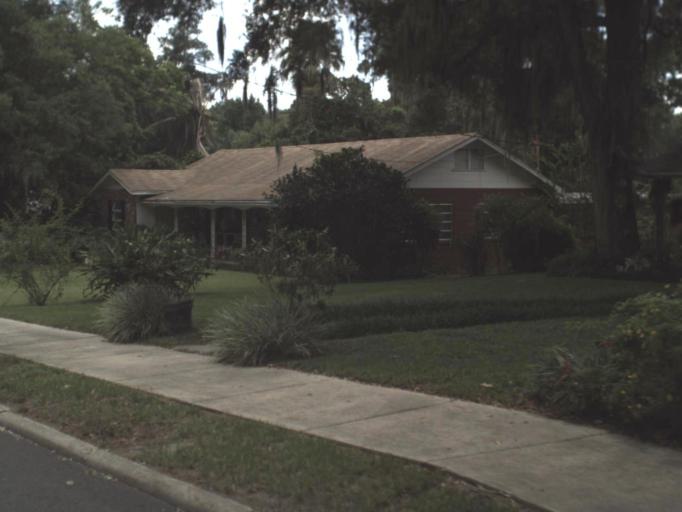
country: US
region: Florida
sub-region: Pasco County
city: Dade City
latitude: 28.3646
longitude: -82.2029
